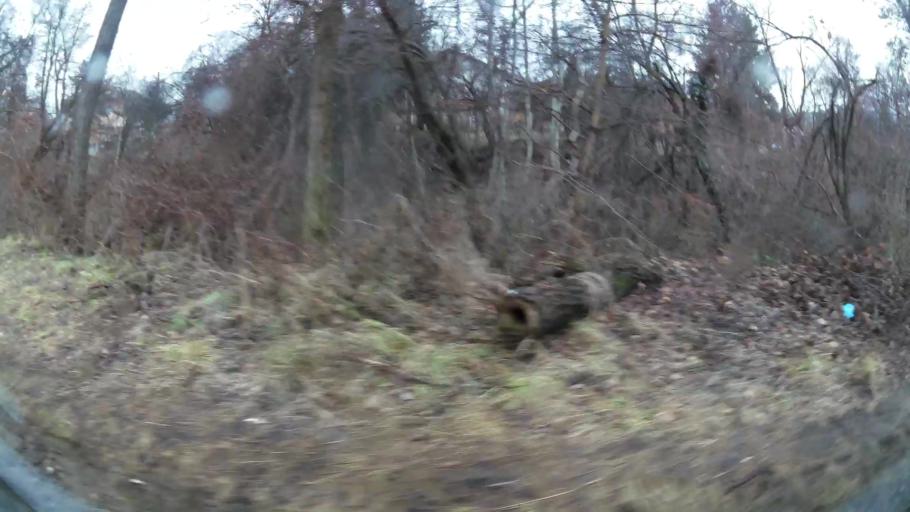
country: BG
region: Sofia-Capital
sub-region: Stolichna Obshtina
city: Sofia
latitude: 42.6133
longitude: 23.3684
